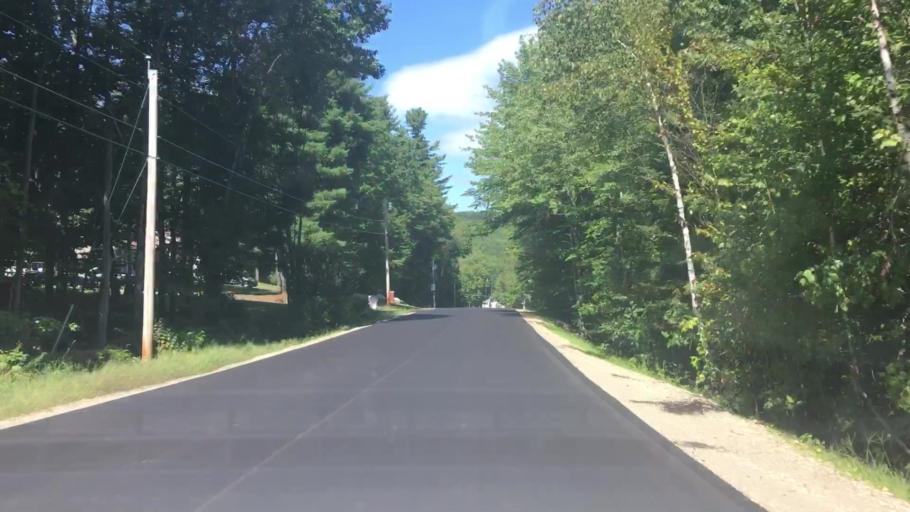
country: US
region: Maine
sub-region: Androscoggin County
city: Sabattus
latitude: 44.1330
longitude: -70.0194
